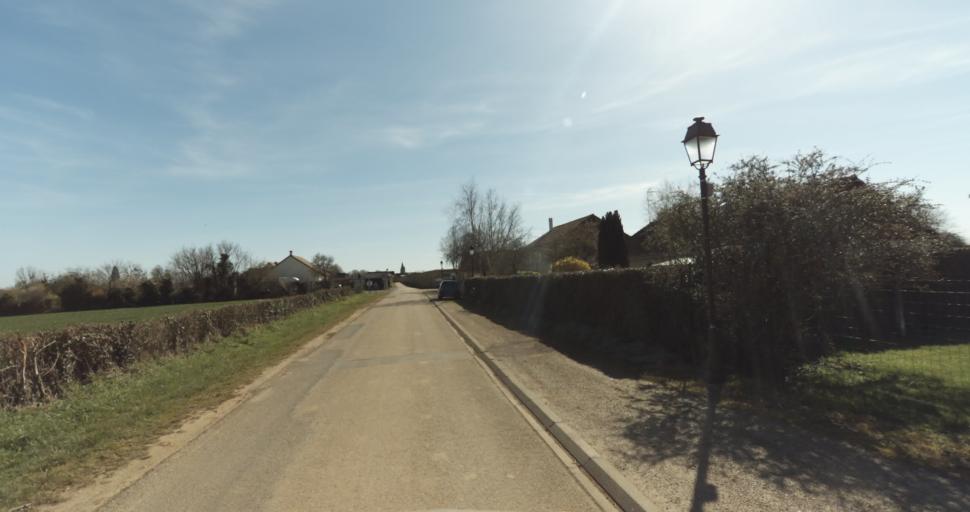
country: FR
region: Lower Normandy
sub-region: Departement du Calvados
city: Saint-Pierre-sur-Dives
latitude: 49.0428
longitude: -0.0262
